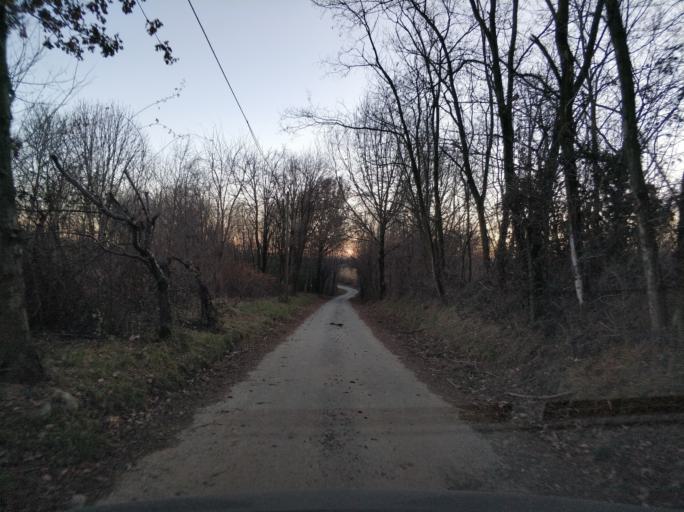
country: IT
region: Piedmont
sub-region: Provincia di Torino
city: Vauda Canavese Superiore
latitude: 45.2700
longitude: 7.6068
